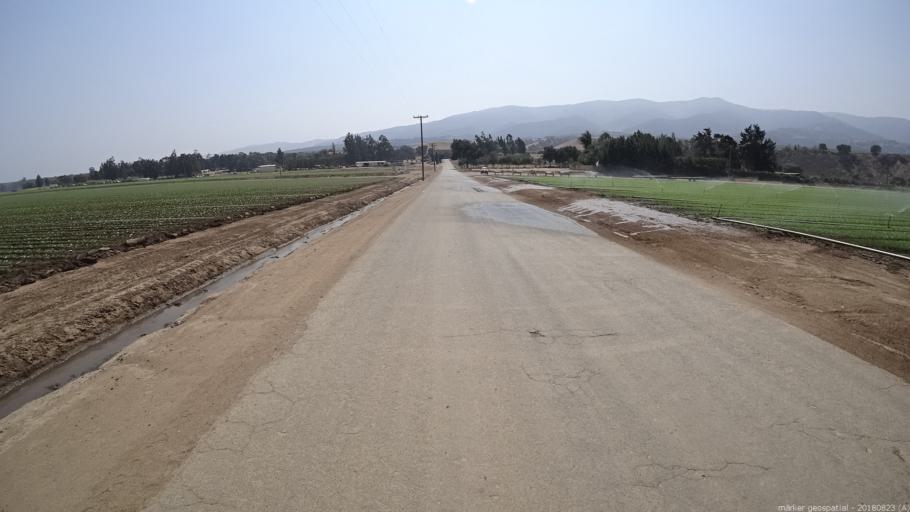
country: US
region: California
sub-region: Monterey County
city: Soledad
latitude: 36.3965
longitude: -121.3649
